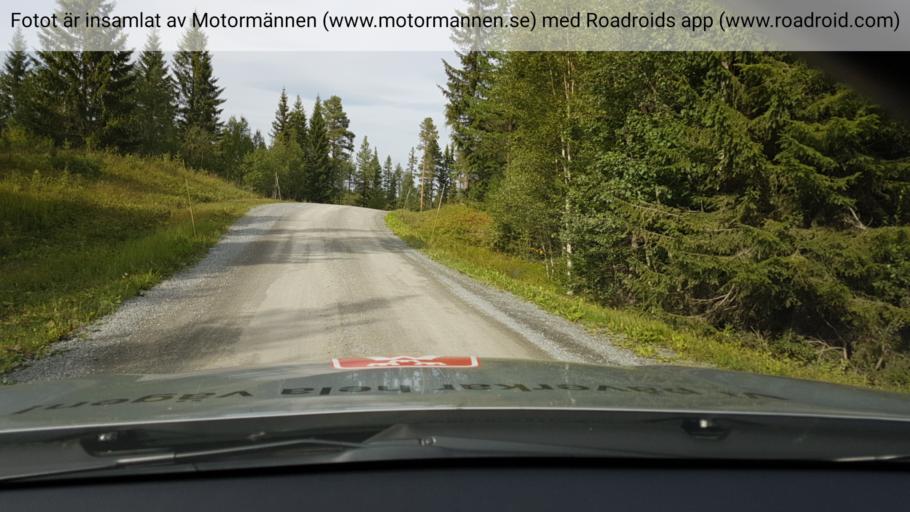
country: SE
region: Jaemtland
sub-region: Krokoms Kommun
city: Valla
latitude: 63.4051
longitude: 14.0859
